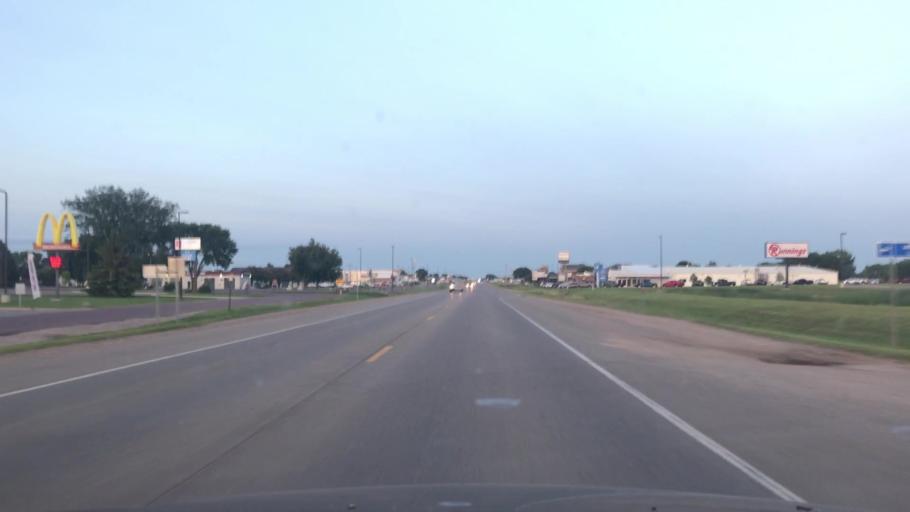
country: US
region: Minnesota
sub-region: Redwood County
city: Redwood Falls
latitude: 44.5414
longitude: -95.0982
